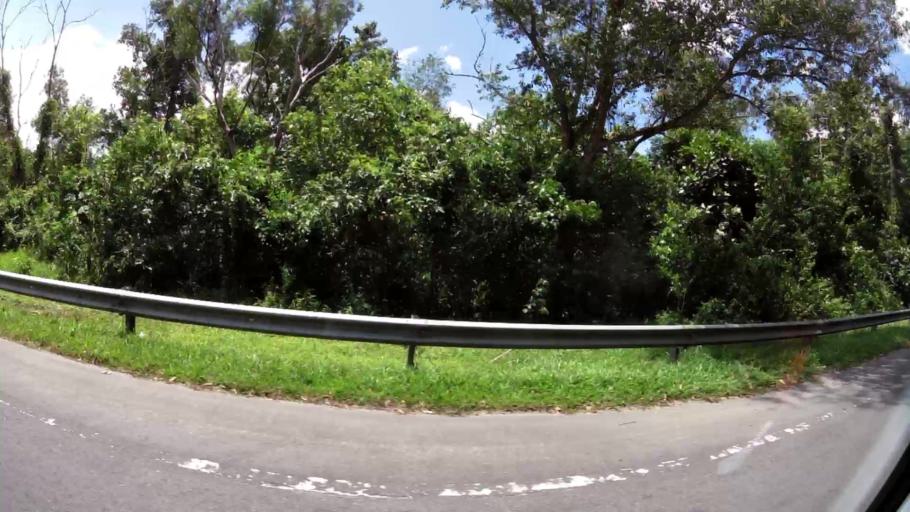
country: BN
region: Brunei and Muara
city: Bandar Seri Begawan
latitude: 4.9265
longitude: 114.9589
